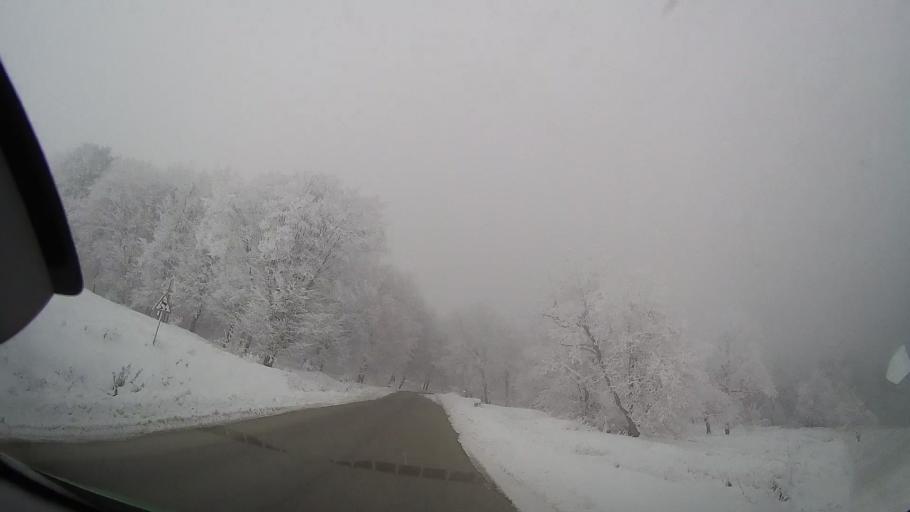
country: RO
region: Neamt
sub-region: Comuna Valea Ursului
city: Valea Ursului
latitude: 46.8370
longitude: 27.0702
